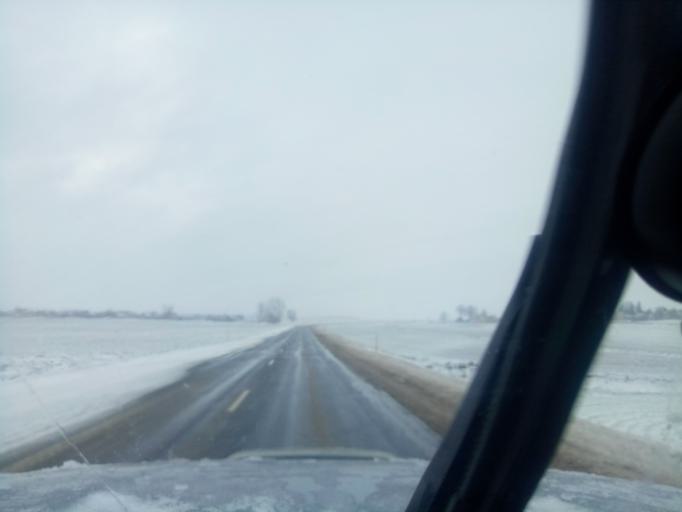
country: BY
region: Minsk
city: Haradzyeya
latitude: 53.3075
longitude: 26.5700
